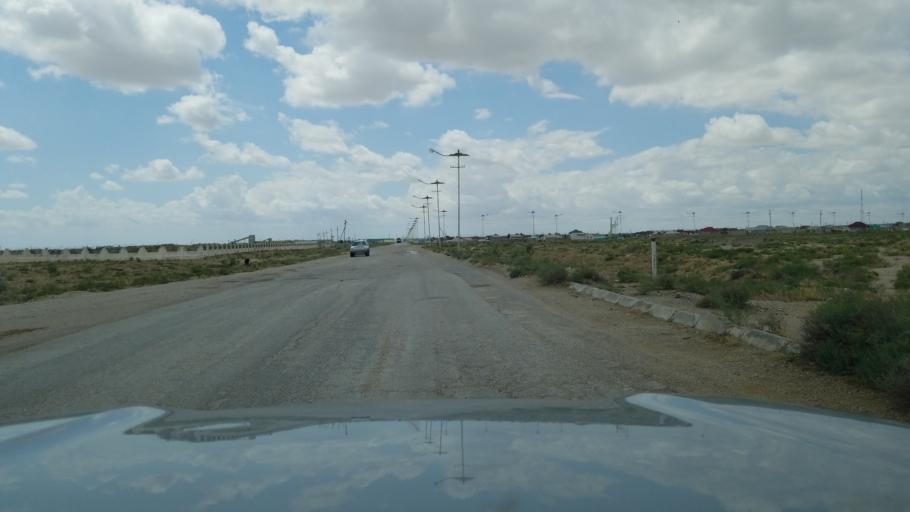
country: TM
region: Balkan
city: Balkanabat
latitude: 39.4897
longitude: 54.3994
